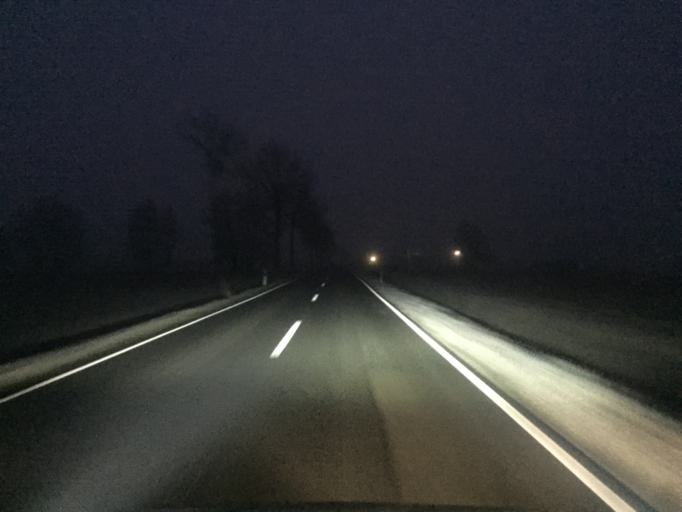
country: DE
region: Lower Saxony
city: Maasen
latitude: 52.6687
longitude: 8.8915
